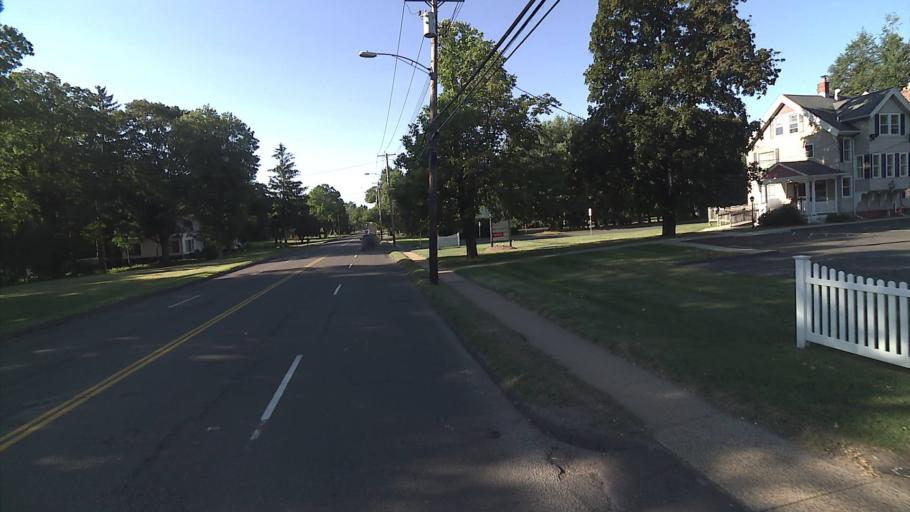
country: US
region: Connecticut
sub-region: New Haven County
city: Hamden
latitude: 41.4119
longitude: -72.9014
